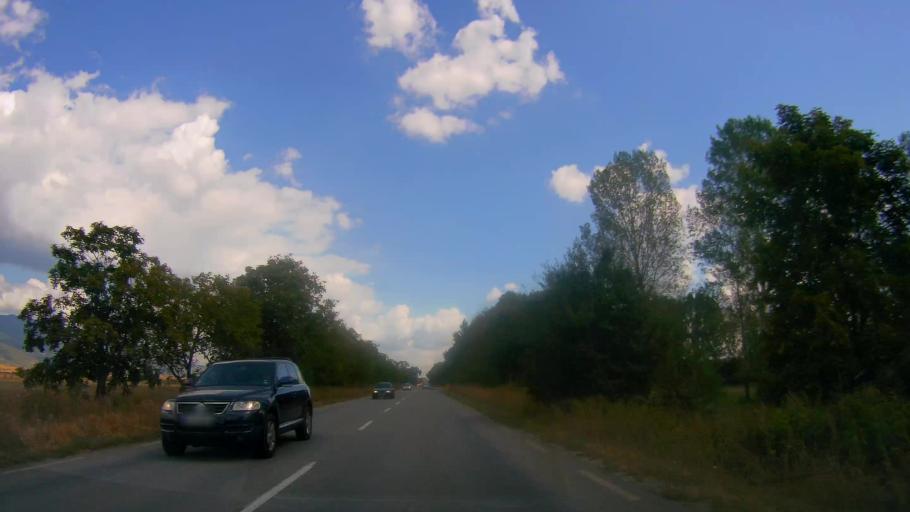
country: BG
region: Sliven
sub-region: Obshtina Tvurditsa
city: Tvurditsa
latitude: 42.6570
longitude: 25.9046
